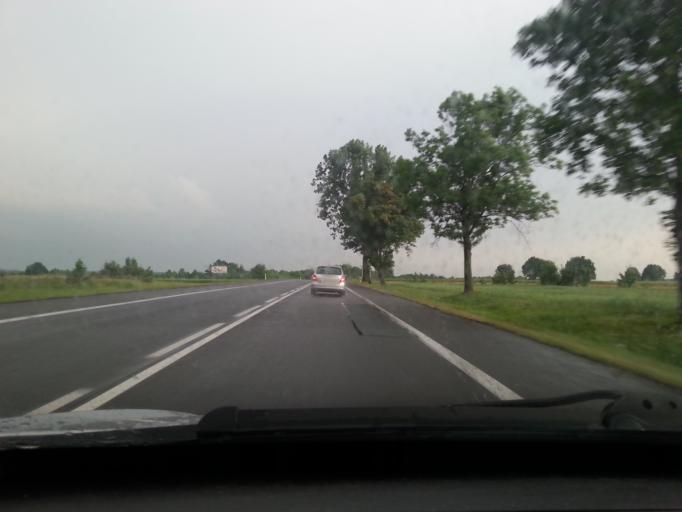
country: PL
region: Lodz Voivodeship
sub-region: Powiat zgierski
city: Strykow
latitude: 51.8507
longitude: 19.5620
